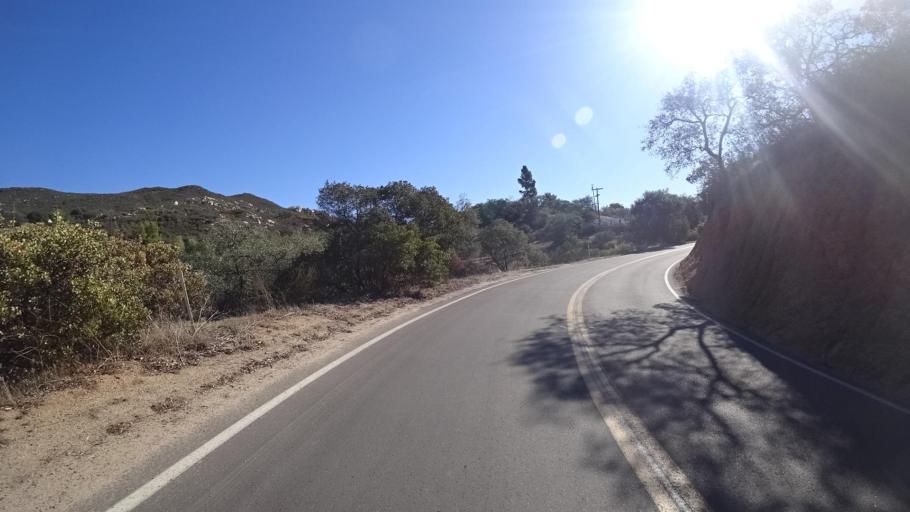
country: MX
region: Baja California
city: Tecate
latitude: 32.6763
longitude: -116.7192
